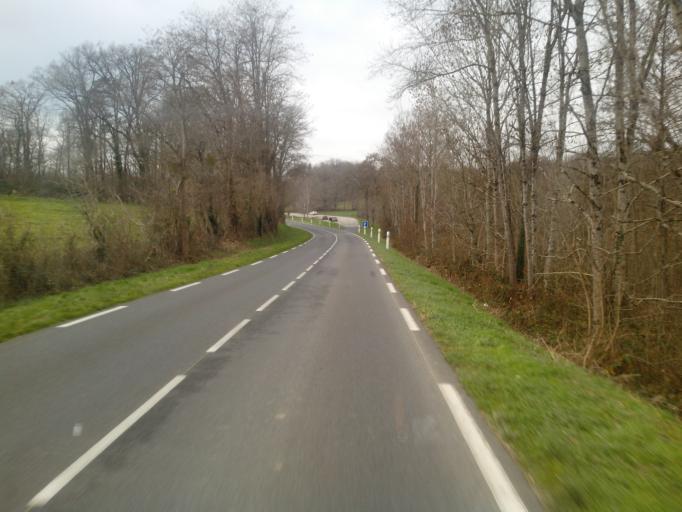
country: FR
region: Limousin
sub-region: Departement de la Haute-Vienne
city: Magnac-Laval
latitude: 46.2145
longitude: 1.1427
